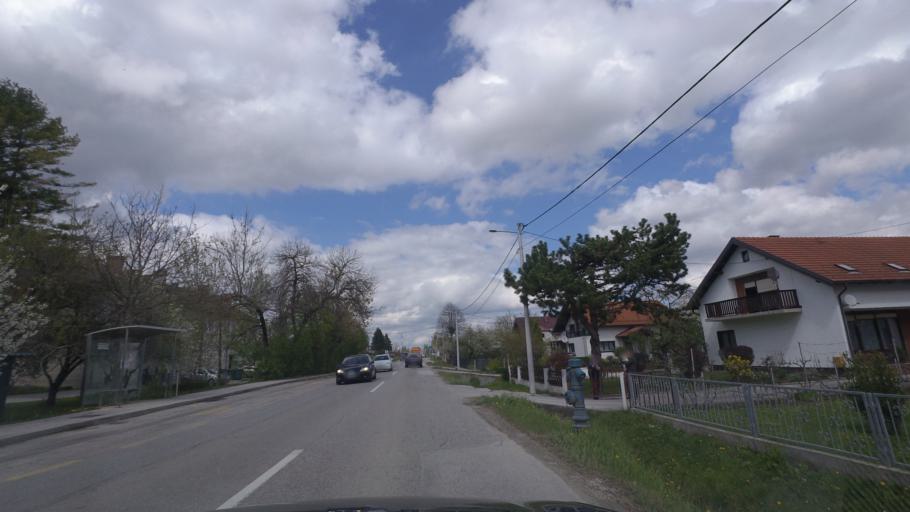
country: HR
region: Zagrebacka
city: Kerestinec
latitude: 45.7611
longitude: 15.8064
